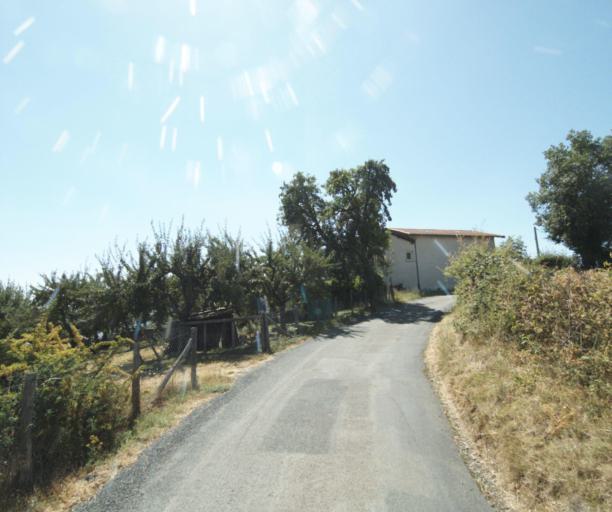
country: FR
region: Rhone-Alpes
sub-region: Departement du Rhone
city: Bessenay
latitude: 45.7811
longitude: 4.5250
